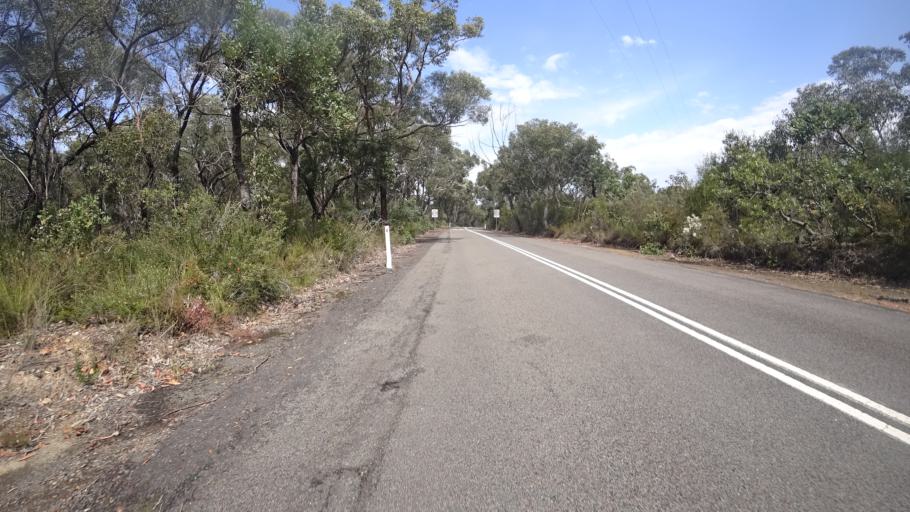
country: AU
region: New South Wales
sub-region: Hornsby Shire
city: Mount Colah
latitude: -33.6775
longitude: 151.1278
